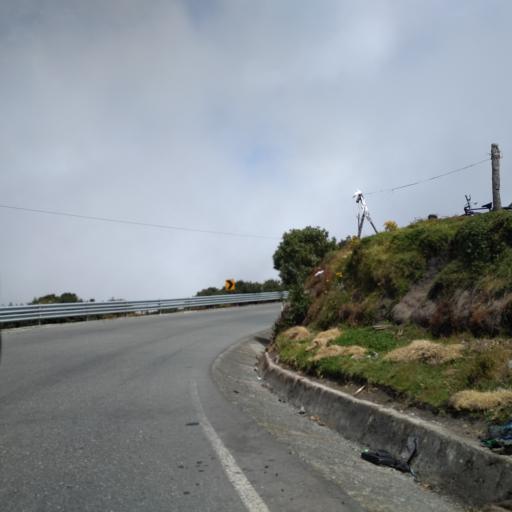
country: EC
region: Cotopaxi
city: La Mana
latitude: -0.9875
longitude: -78.9641
